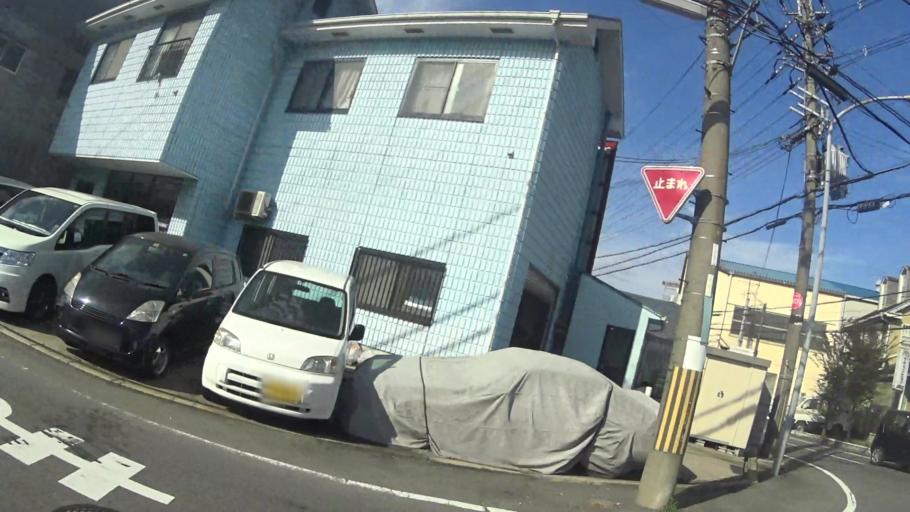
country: JP
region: Kyoto
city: Yawata
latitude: 34.8659
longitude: 135.7291
